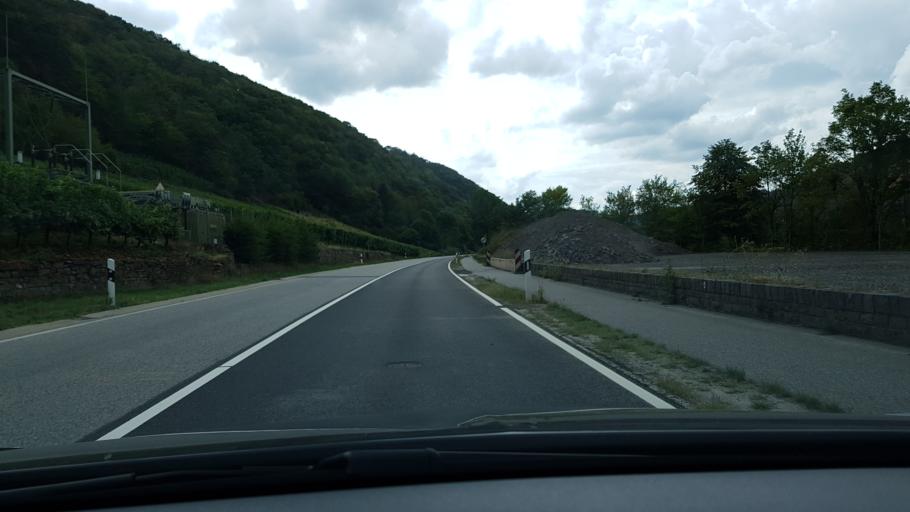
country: DE
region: Rheinland-Pfalz
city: Niederfell
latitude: 50.2736
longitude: 7.4604
